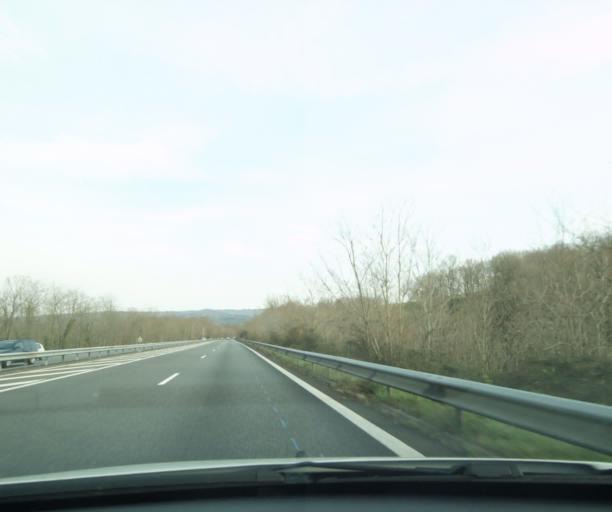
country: FR
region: Midi-Pyrenees
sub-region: Departement des Hautes-Pyrenees
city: Tournay
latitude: 43.1997
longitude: 0.2059
